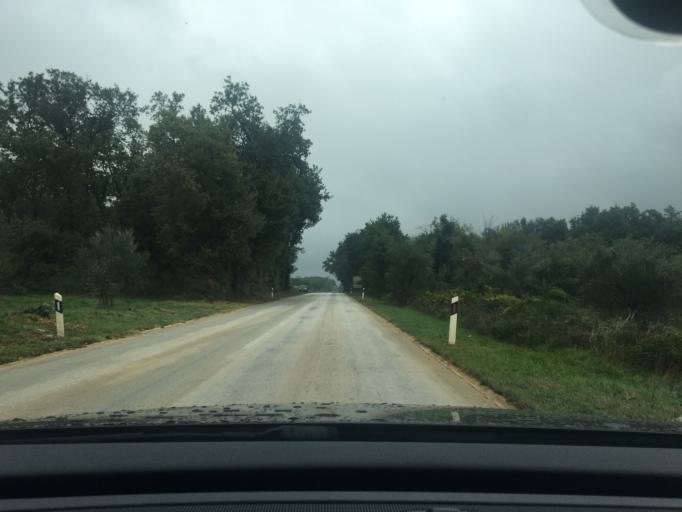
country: HR
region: Istarska
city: Novigrad
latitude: 45.3608
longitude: 13.6057
